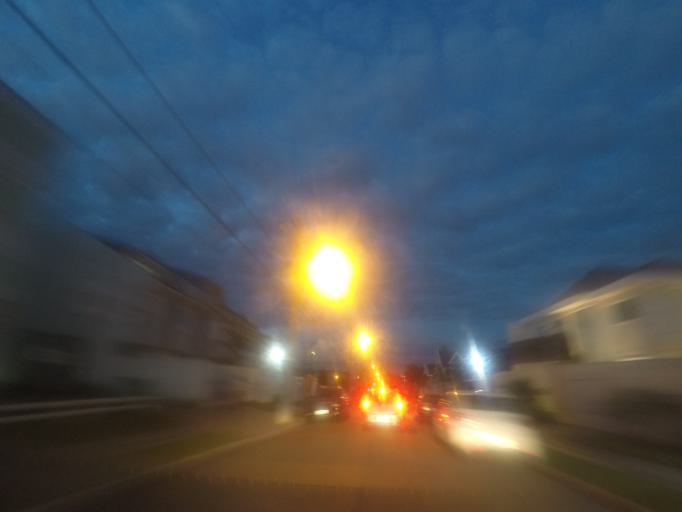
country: BR
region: Parana
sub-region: Pinhais
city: Pinhais
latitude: -25.3859
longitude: -49.2075
